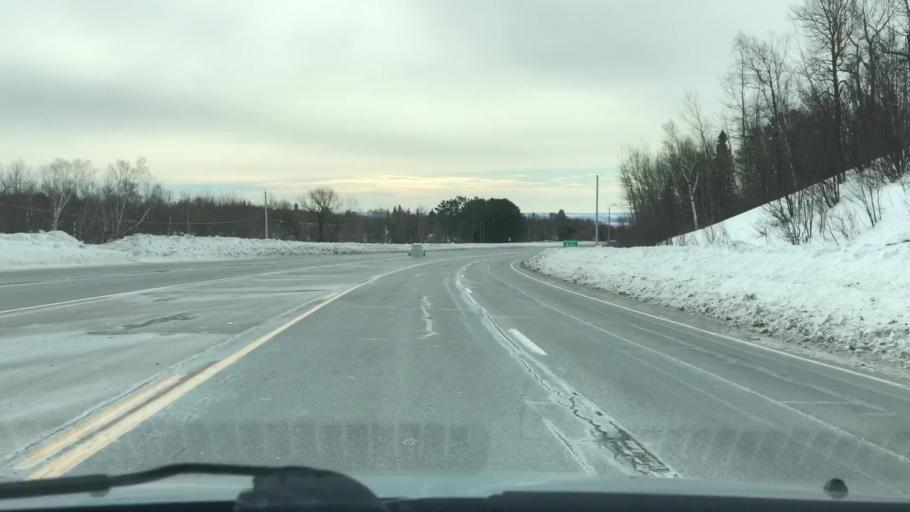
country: US
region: Minnesota
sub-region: Saint Louis County
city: Duluth
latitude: 46.7857
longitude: -92.1408
